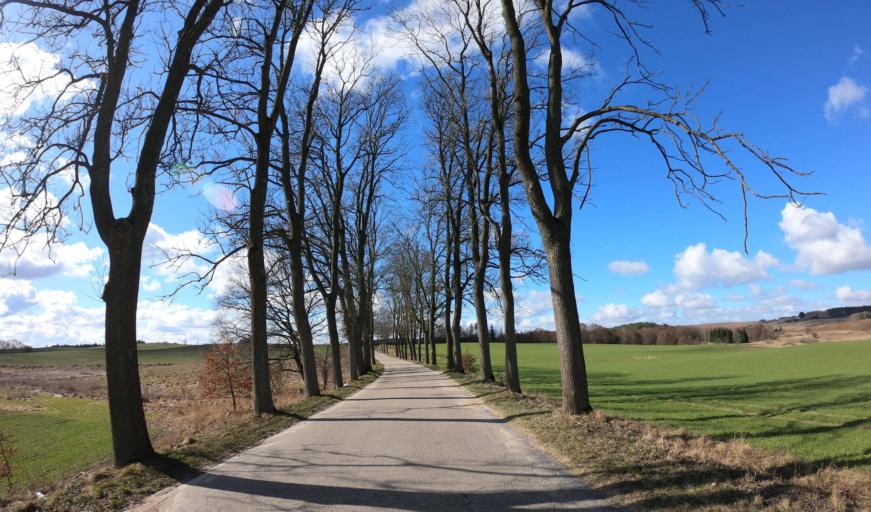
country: PL
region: West Pomeranian Voivodeship
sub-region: Powiat drawski
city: Zlocieniec
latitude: 53.4626
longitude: 15.9607
